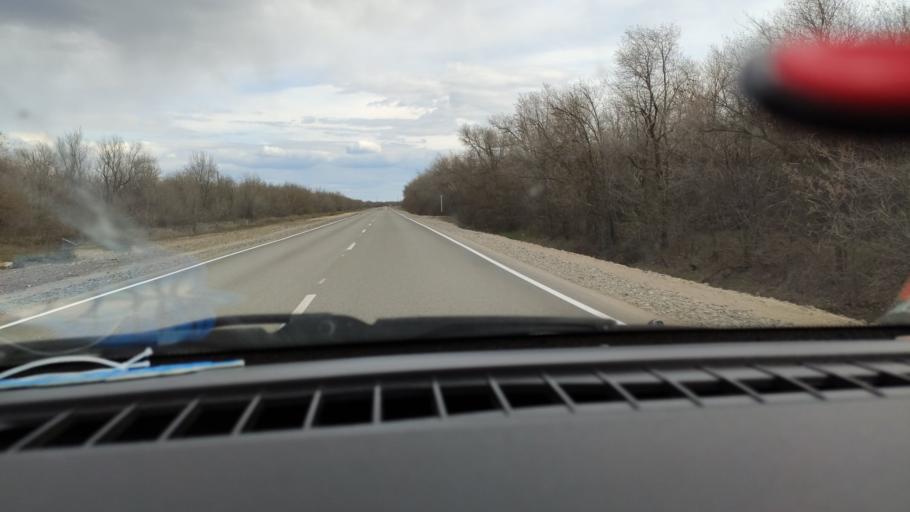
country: RU
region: Saratov
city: Privolzhskiy
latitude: 51.1615
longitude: 45.9547
